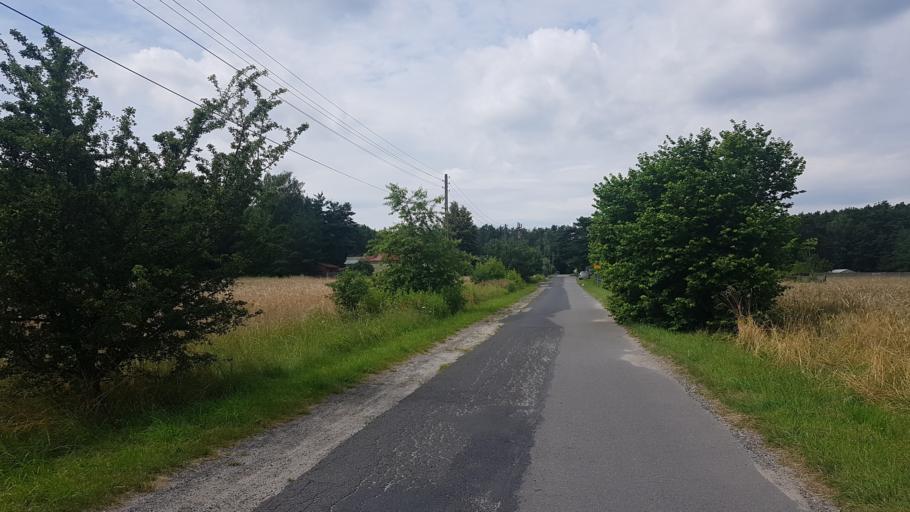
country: PL
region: Opole Voivodeship
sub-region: Powiat opolski
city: Ozimek
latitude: 50.7027
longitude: 18.1453
